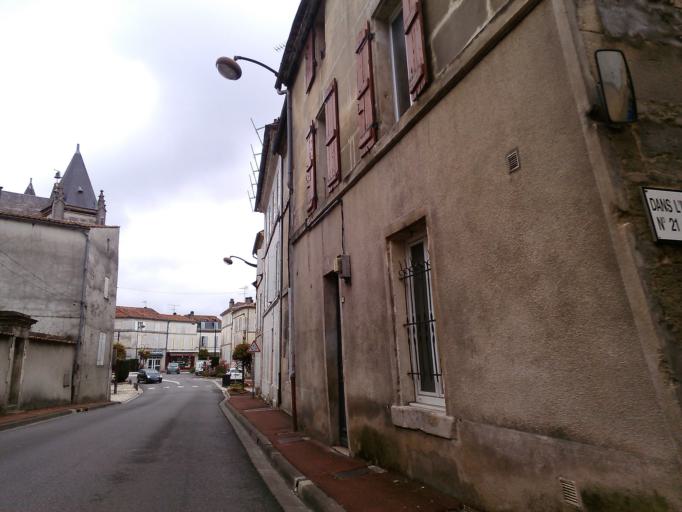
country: FR
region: Poitou-Charentes
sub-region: Departement de la Charente
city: Cognac
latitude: 45.6993
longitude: -0.3345
